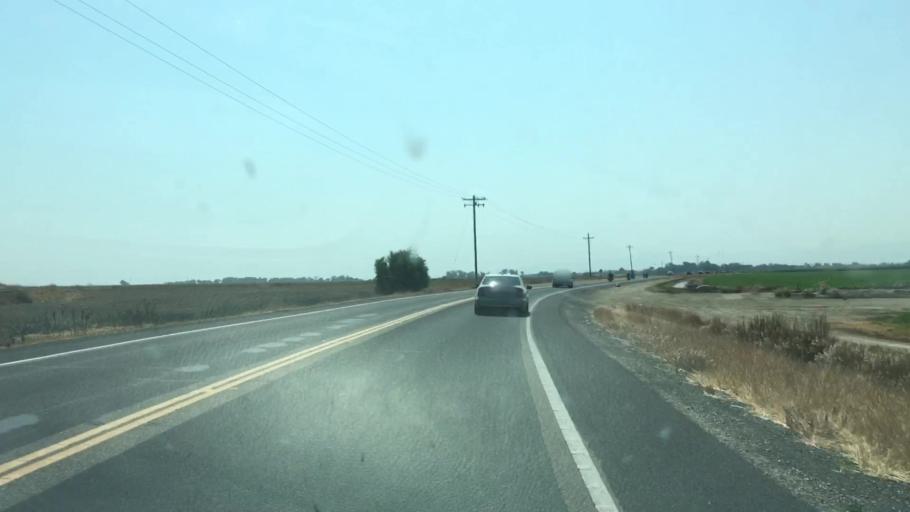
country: US
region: California
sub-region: San Joaquin County
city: Tracy
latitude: 37.8401
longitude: -121.4518
